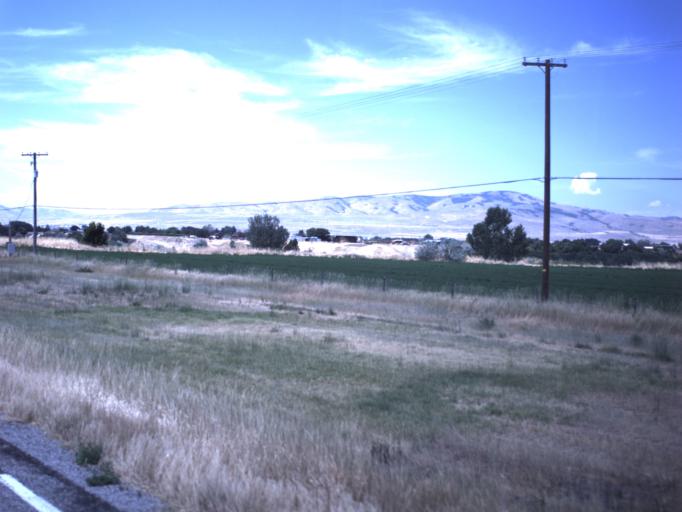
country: US
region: Utah
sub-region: Box Elder County
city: Elwood
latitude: 41.7150
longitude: -112.1056
